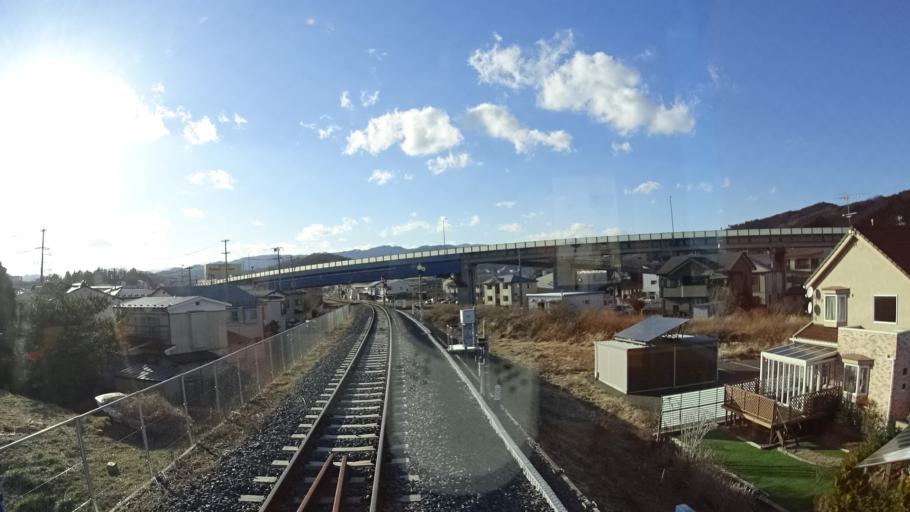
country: JP
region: Iwate
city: Miyako
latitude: 39.6386
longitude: 141.9532
